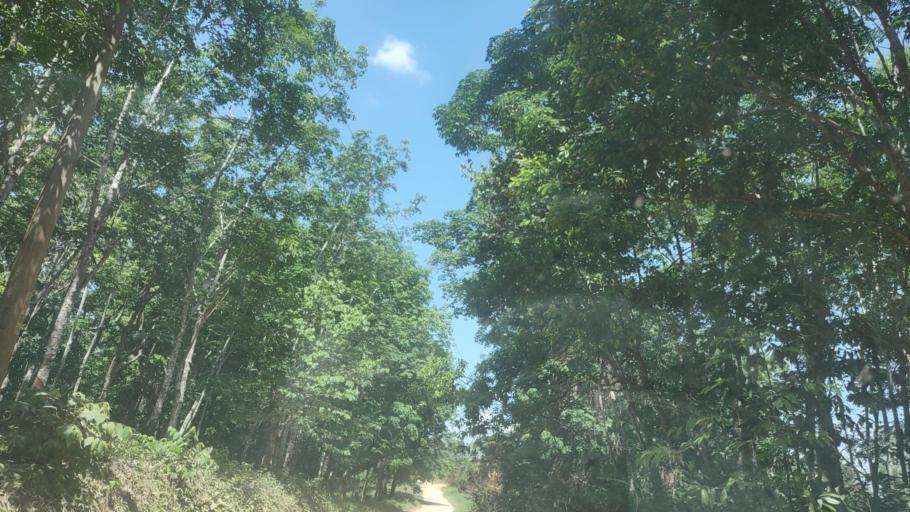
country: MX
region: Veracruz
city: Las Choapas
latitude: 17.7922
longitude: -94.1488
